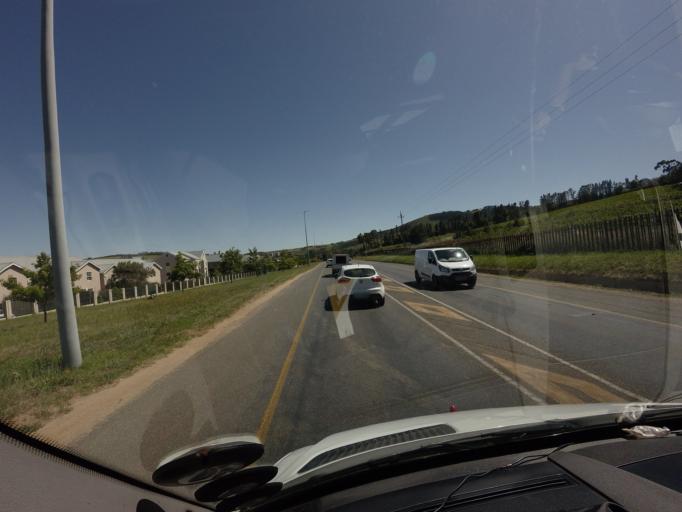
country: ZA
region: Western Cape
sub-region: Cape Winelands District Municipality
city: Stellenbosch
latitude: -33.9029
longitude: 18.8590
